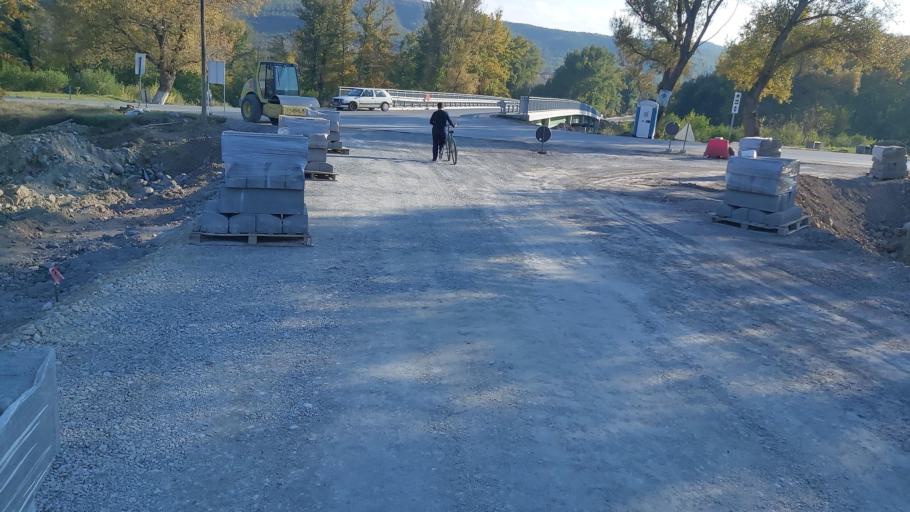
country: MK
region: Demir Kapija
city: Demir Kapija
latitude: 41.4069
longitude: 22.2429
